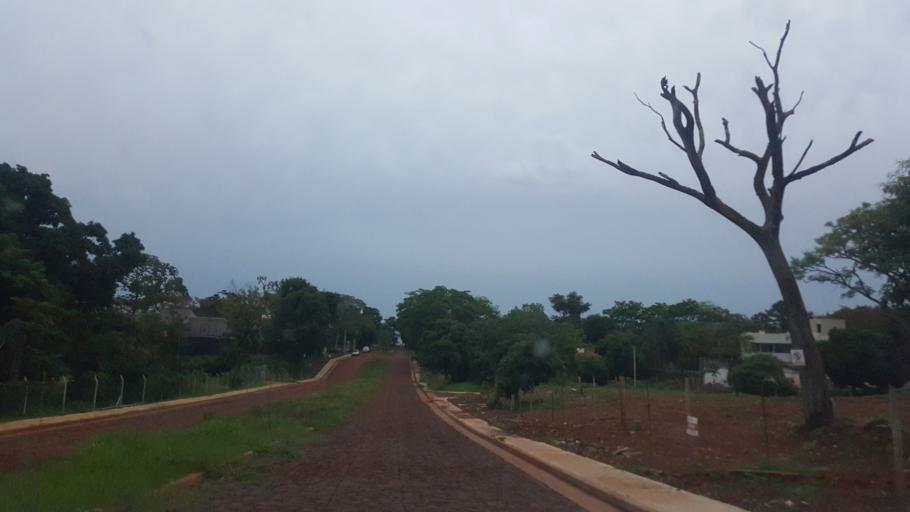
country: AR
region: Misiones
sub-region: Departamento de Capital
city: Posadas
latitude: -27.3572
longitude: -55.9227
